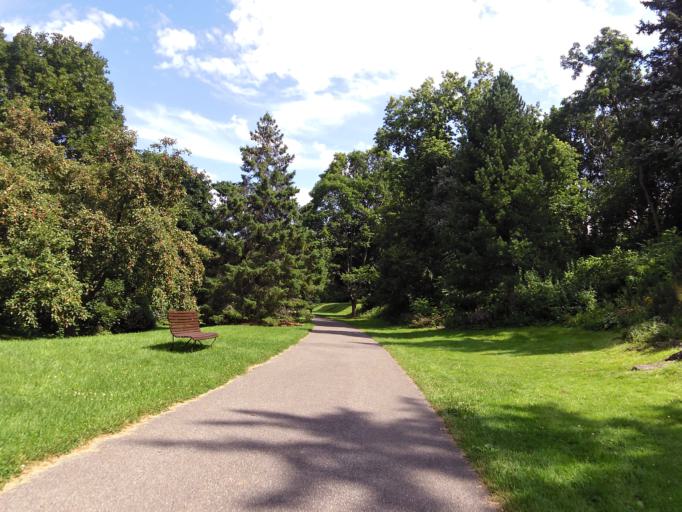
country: CA
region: Quebec
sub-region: Outaouais
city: Gatineau
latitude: 45.4550
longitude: -75.6780
